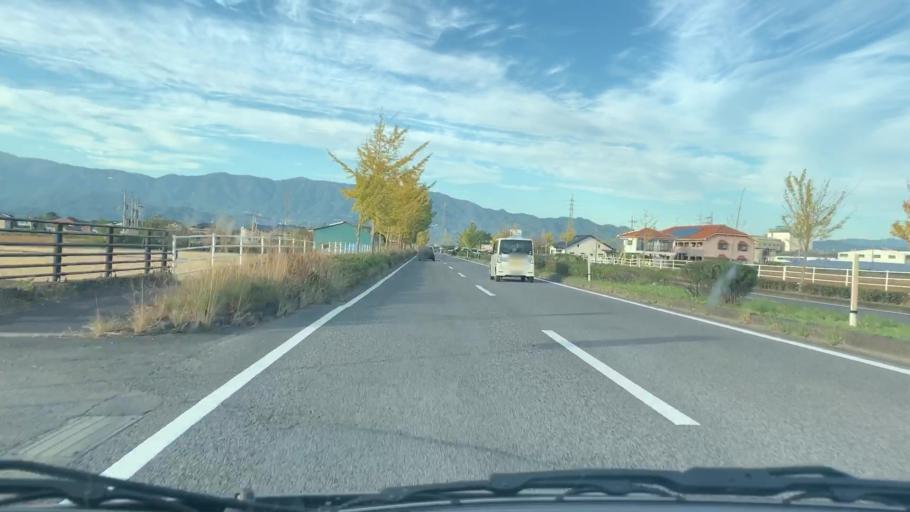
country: JP
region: Saga Prefecture
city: Saga-shi
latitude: 33.2509
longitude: 130.1987
